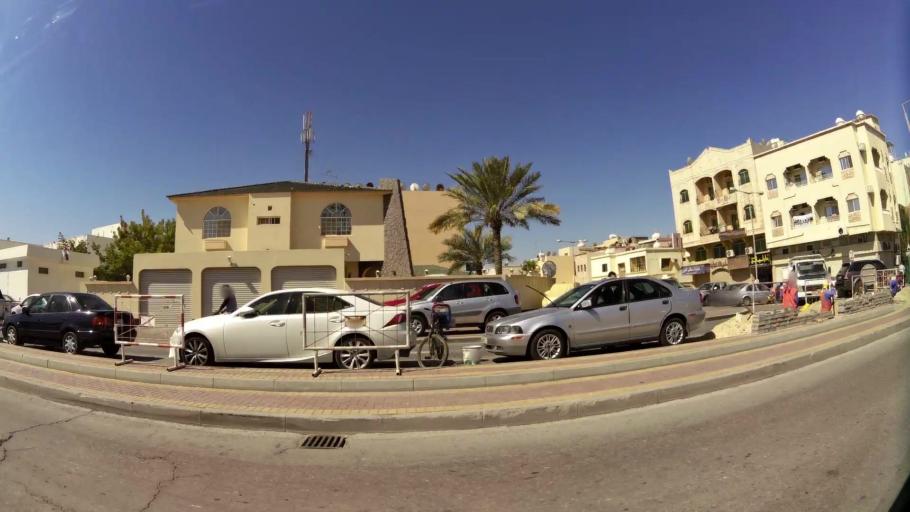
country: BH
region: Muharraq
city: Al Muharraq
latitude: 26.2552
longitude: 50.6197
